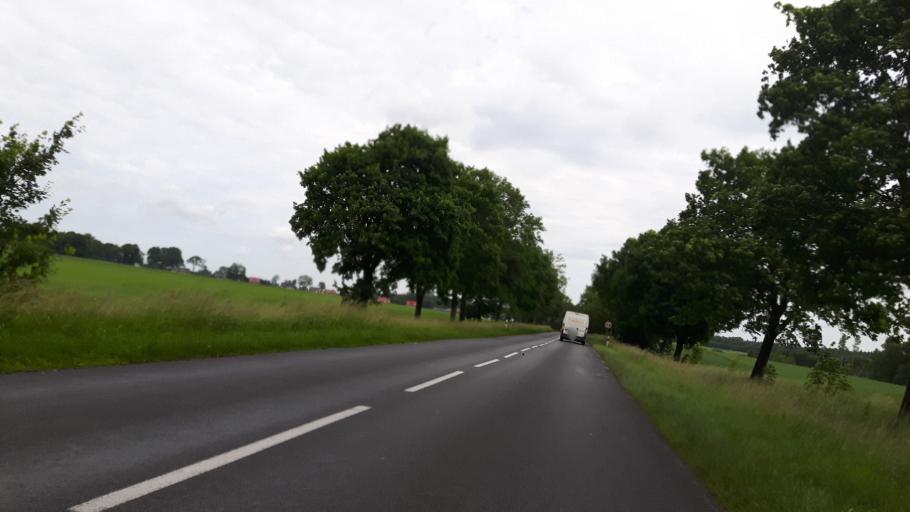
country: PL
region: West Pomeranian Voivodeship
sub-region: Powiat gryficki
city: Gryfice
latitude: 53.9346
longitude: 15.2144
